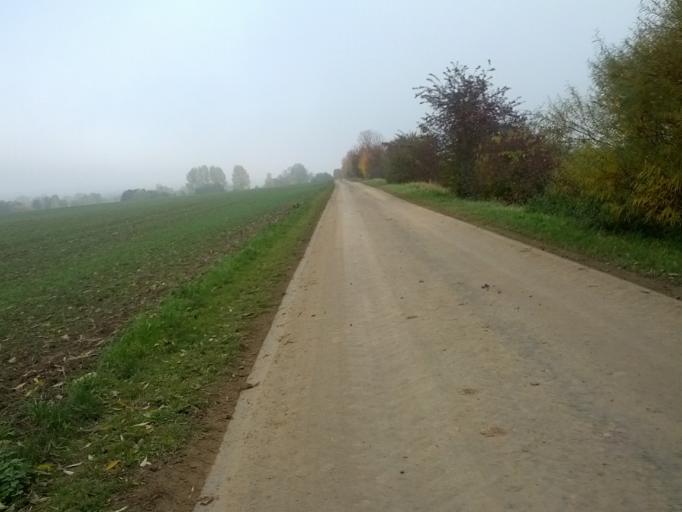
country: DE
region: Thuringia
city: Bischofroda
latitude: 50.9869
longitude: 10.3968
